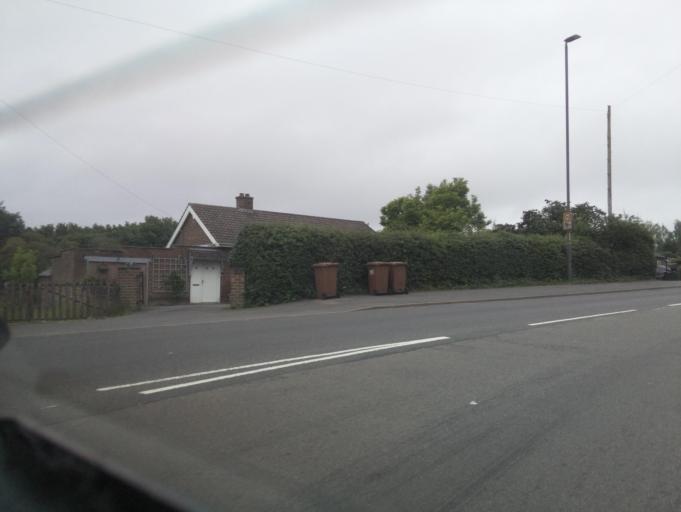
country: GB
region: England
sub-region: Derbyshire
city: Swadlincote
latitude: 52.7667
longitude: -1.5922
